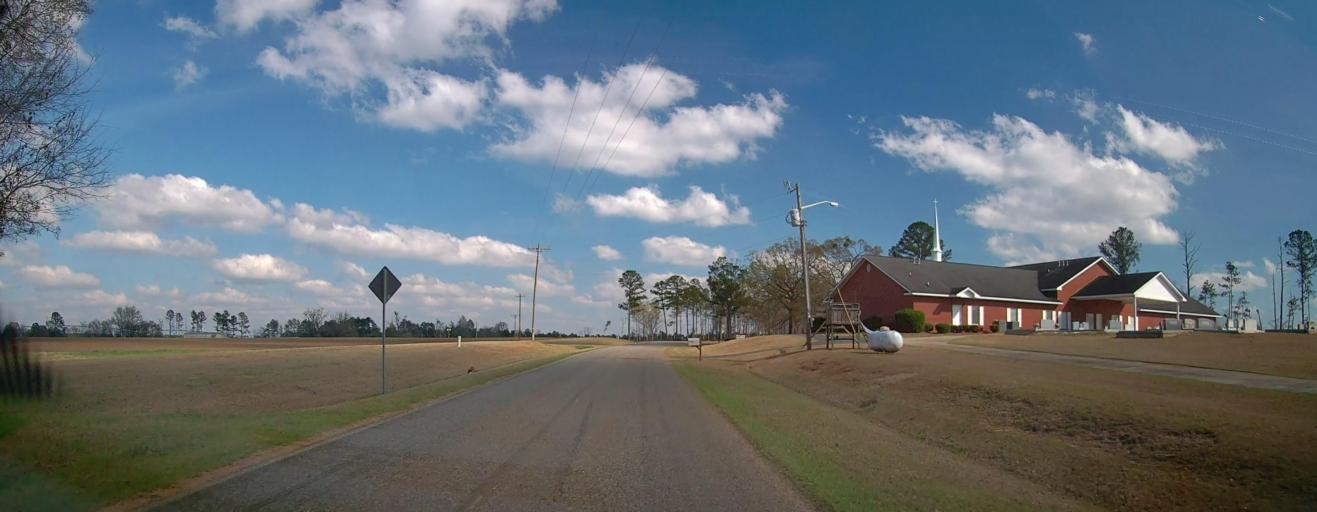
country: US
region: Georgia
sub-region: Wilkinson County
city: Irwinton
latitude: 32.6377
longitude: -83.1564
